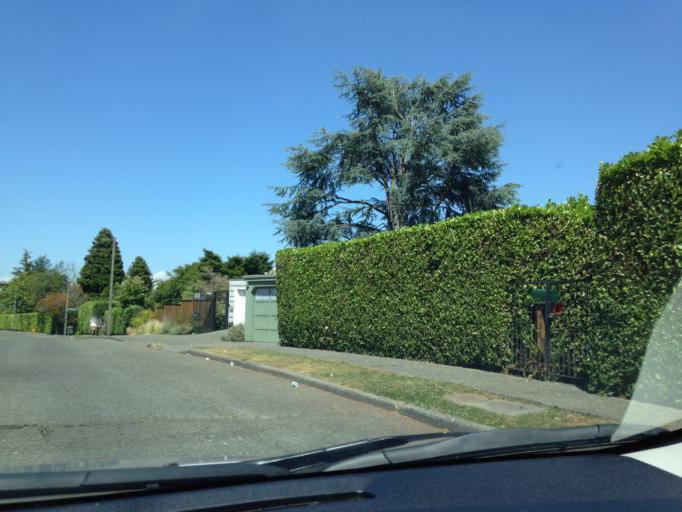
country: US
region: Washington
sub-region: King County
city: Seattle
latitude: 47.5868
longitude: -122.2867
